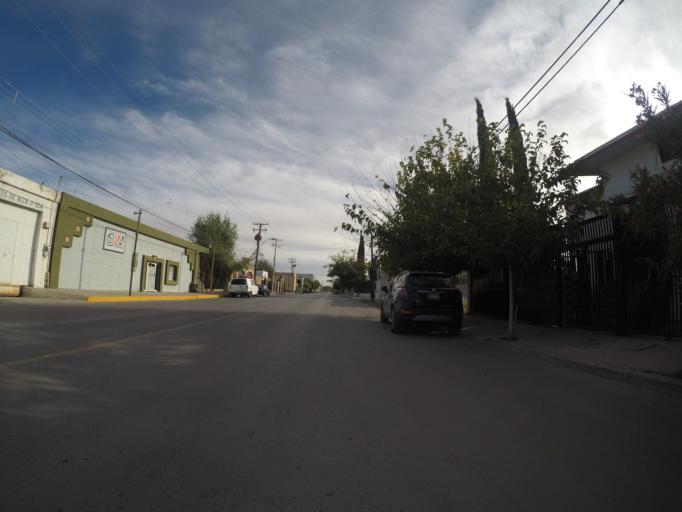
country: MX
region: Chihuahua
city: Ciudad Juarez
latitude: 31.7378
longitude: -106.4290
